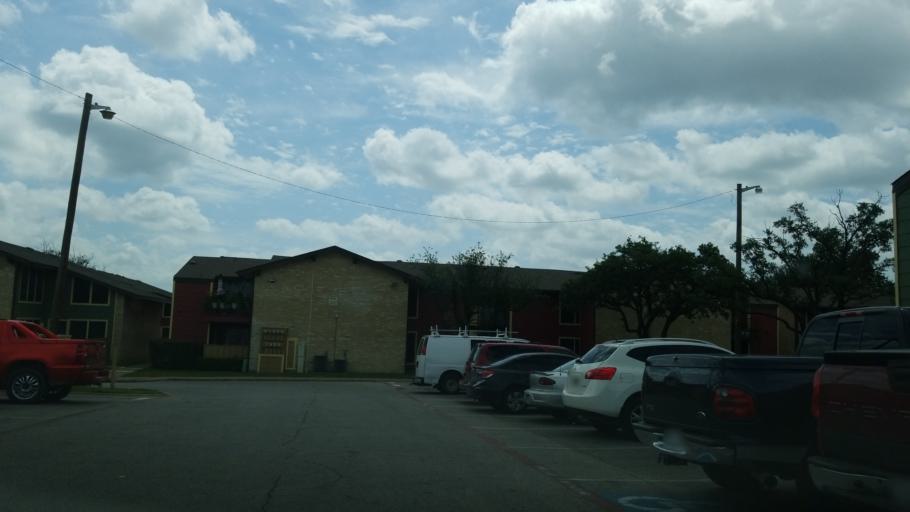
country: US
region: Texas
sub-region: Dallas County
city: Farmers Branch
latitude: 32.8737
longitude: -96.8678
